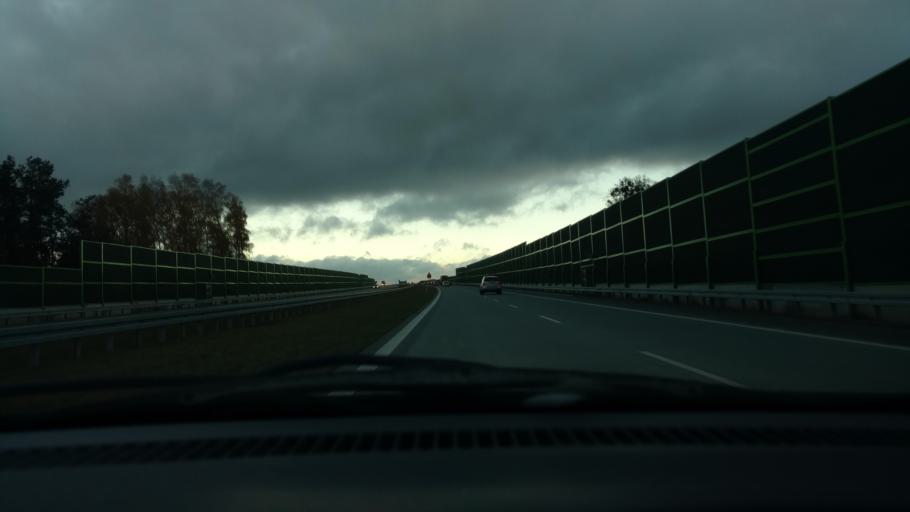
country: PL
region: Lodz Voivodeship
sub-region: Powiat lodzki wschodni
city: Andrespol
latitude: 51.7219
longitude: 19.6078
